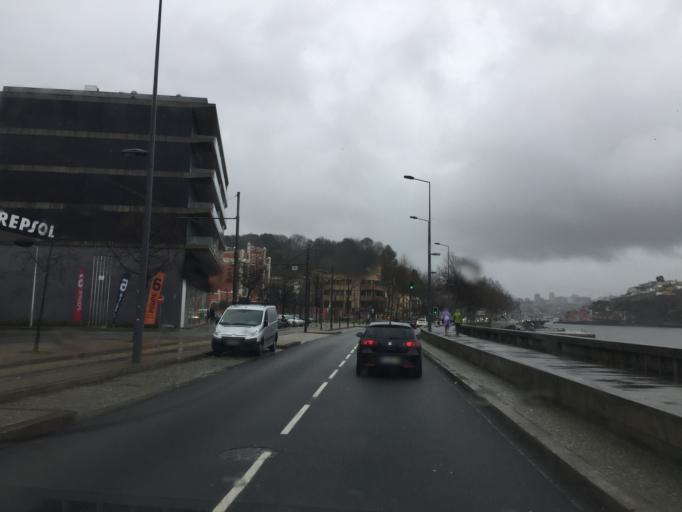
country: PT
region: Porto
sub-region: Vila Nova de Gaia
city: Vila Nova de Gaia
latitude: 41.1479
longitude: -8.6350
